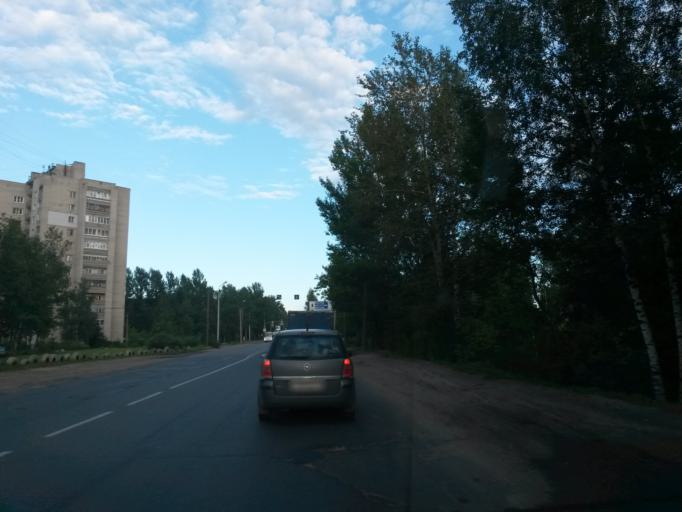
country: RU
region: Jaroslavl
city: Yaroslavl
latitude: 57.5807
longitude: 39.8313
